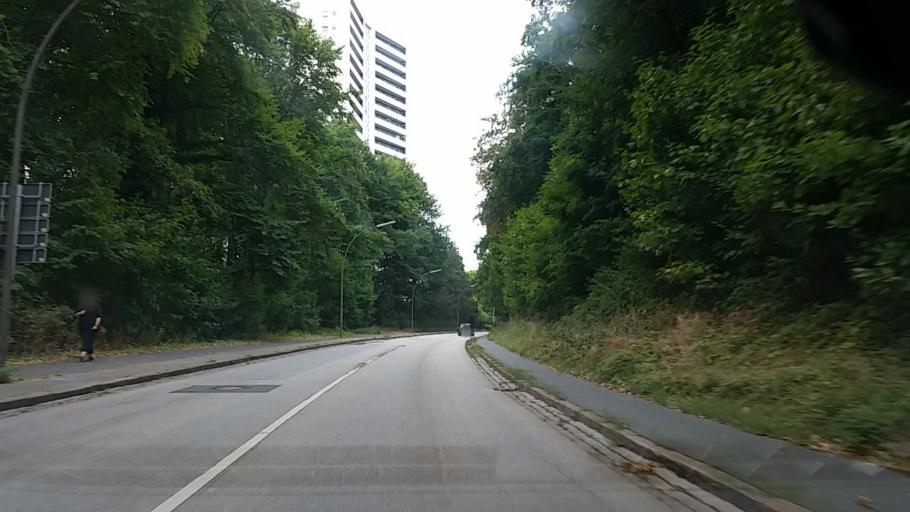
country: DE
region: Schleswig-Holstein
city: Reinbek
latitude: 53.5103
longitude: 10.2384
